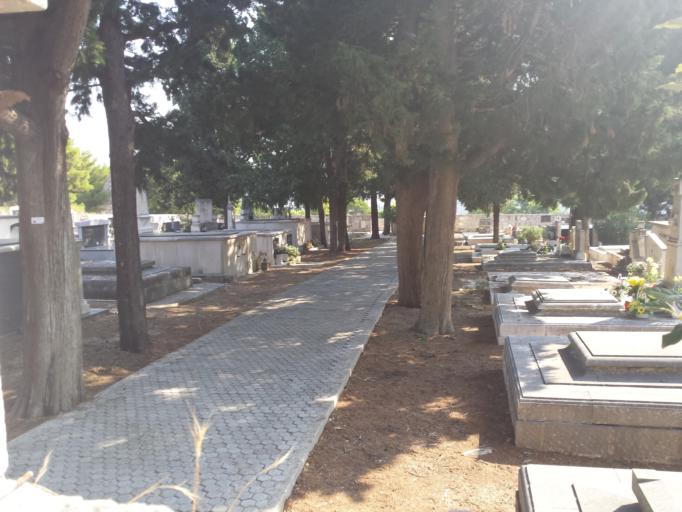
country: HR
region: Sibensko-Kniniska
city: Rogoznica
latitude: 43.5276
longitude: 15.9702
